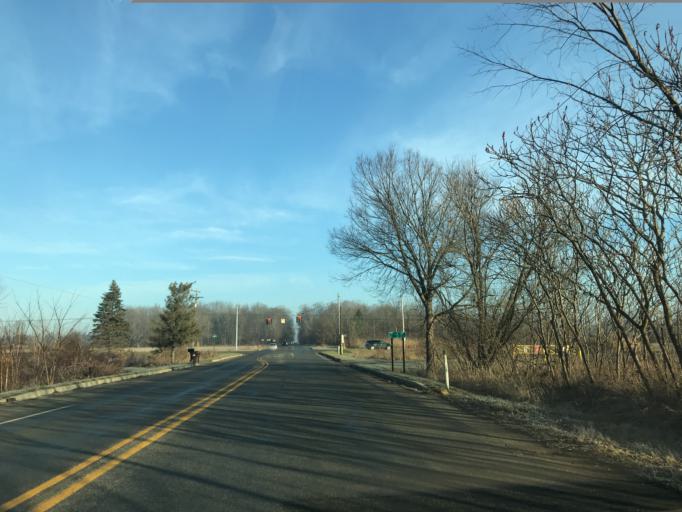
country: US
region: Michigan
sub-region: Eaton County
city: Dimondale
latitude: 42.6391
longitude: -84.6029
